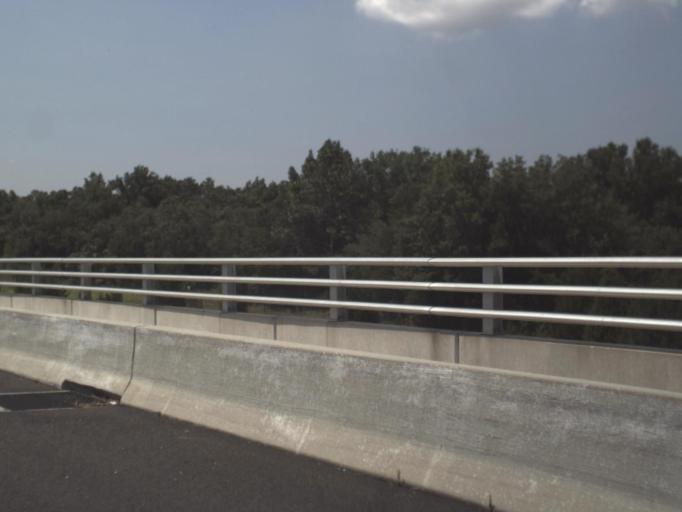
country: US
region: Florida
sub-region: Levy County
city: Inglis
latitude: 29.0113
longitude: -82.6627
